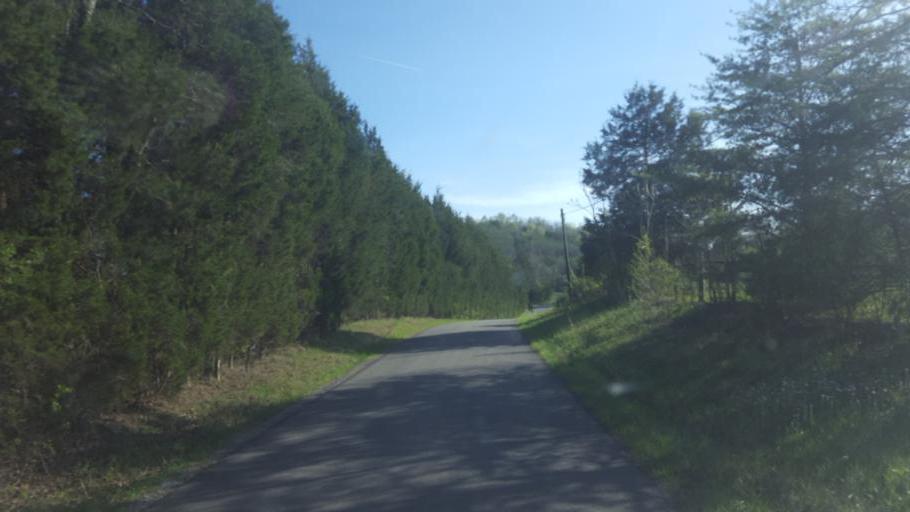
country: US
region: Kentucky
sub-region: Barren County
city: Cave City
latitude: 37.1931
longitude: -86.0130
